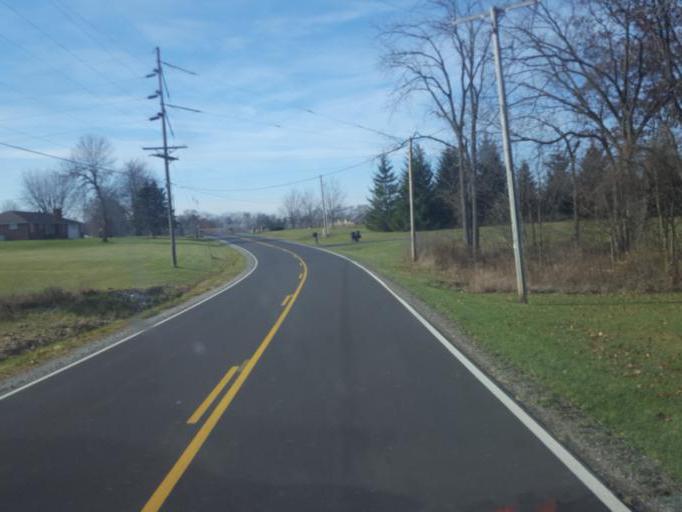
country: US
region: Ohio
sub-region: Crawford County
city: Bucyrus
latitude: 40.8229
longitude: -82.9205
